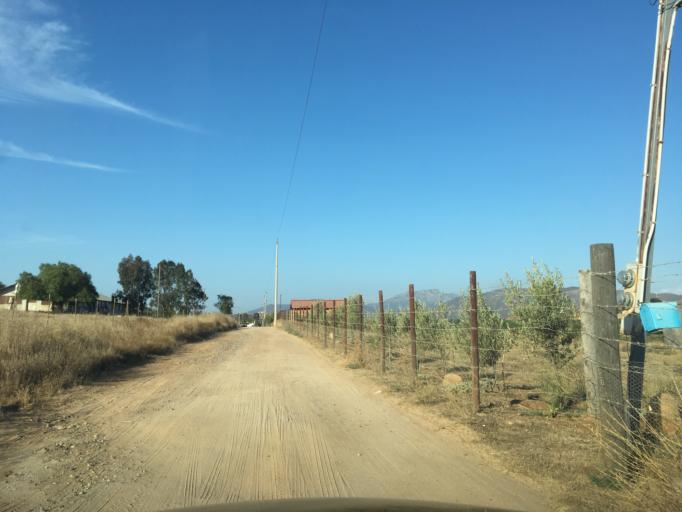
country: MX
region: Baja California
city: El Sauzal
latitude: 32.0172
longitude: -116.6675
